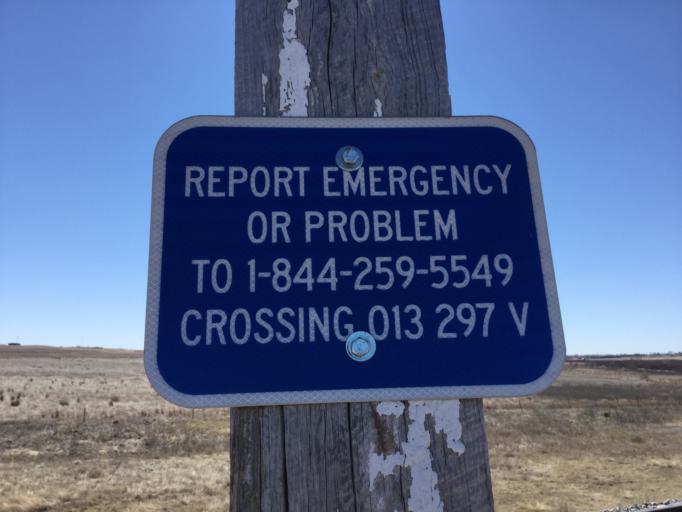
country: US
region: Kansas
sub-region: Grant County
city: Ulysses
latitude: 37.5909
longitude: -101.3201
